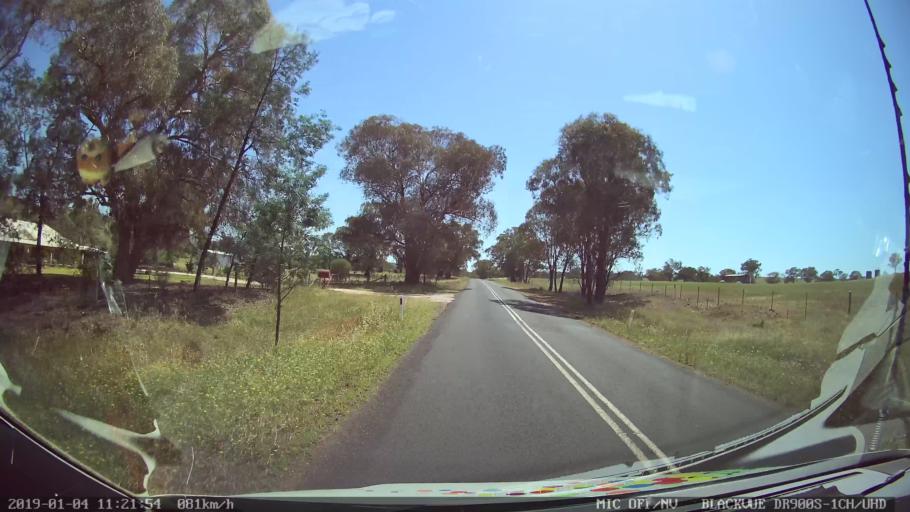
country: AU
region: New South Wales
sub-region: Cabonne
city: Molong
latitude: -33.1507
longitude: 148.7162
